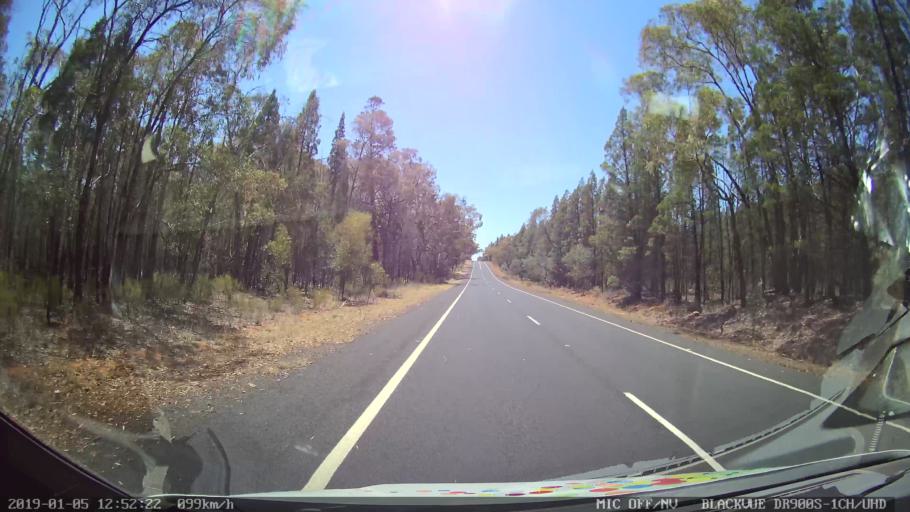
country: AU
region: New South Wales
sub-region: Warrumbungle Shire
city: Coonabarabran
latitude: -31.1213
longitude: 149.6549
